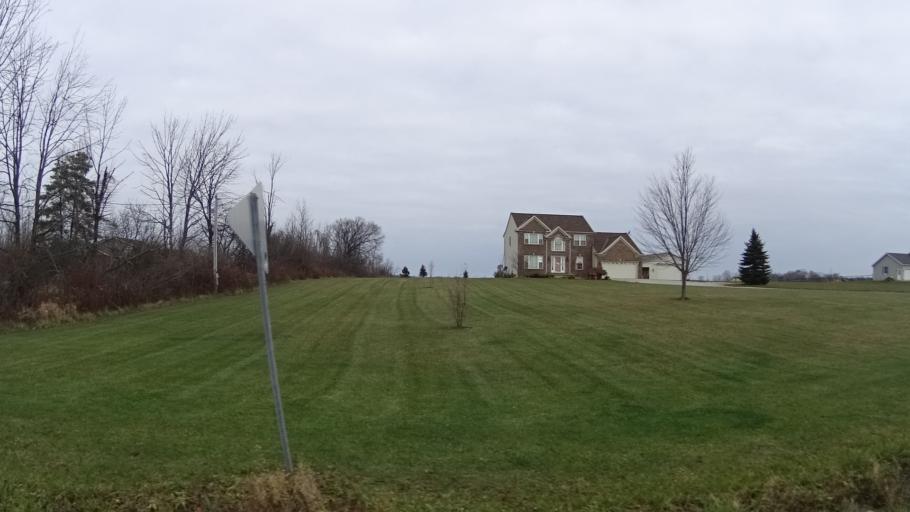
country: US
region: Ohio
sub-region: Lorain County
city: Wellington
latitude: 41.1372
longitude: -82.1773
